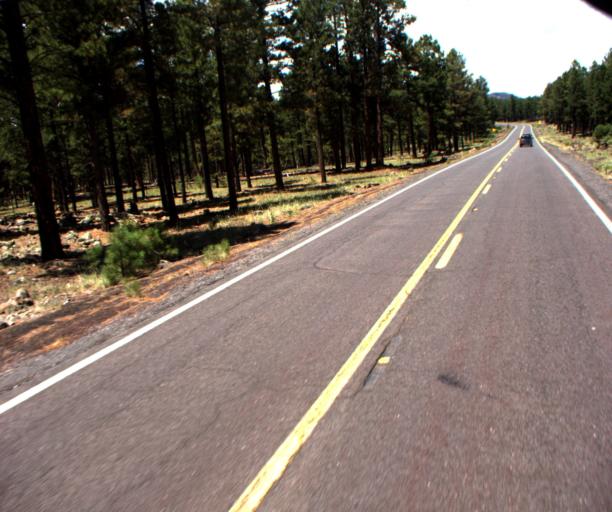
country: US
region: Arizona
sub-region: Coconino County
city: Parks
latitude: 35.4556
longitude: -111.7756
